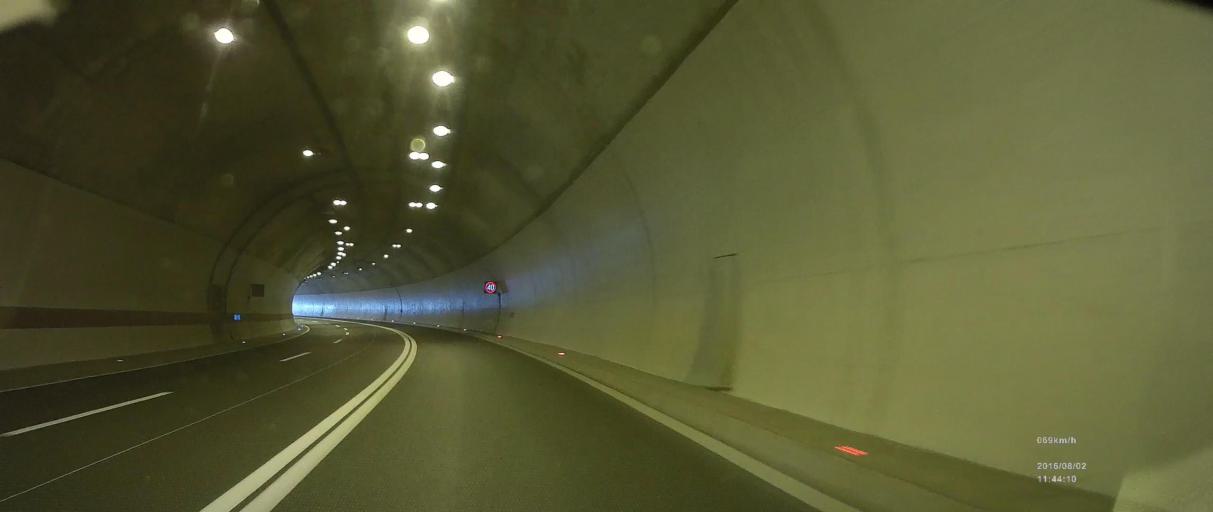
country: HR
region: Dubrovacko-Neretvanska
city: Komin
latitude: 43.0540
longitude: 17.4601
